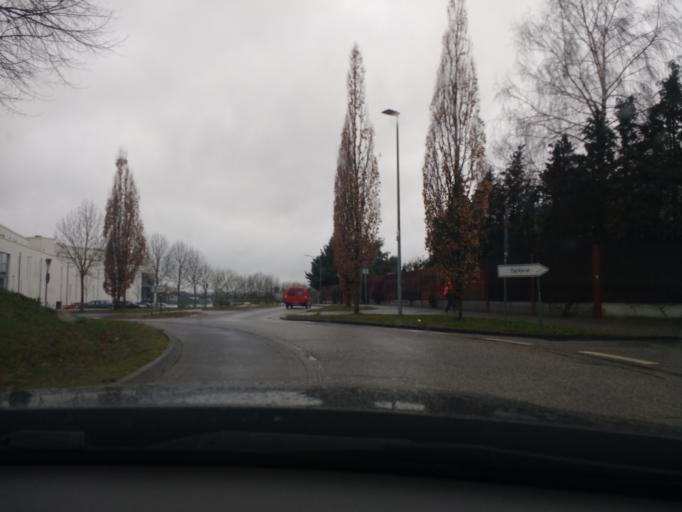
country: DE
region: Rheinland-Pfalz
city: Irsch
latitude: 49.7384
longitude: 6.6985
